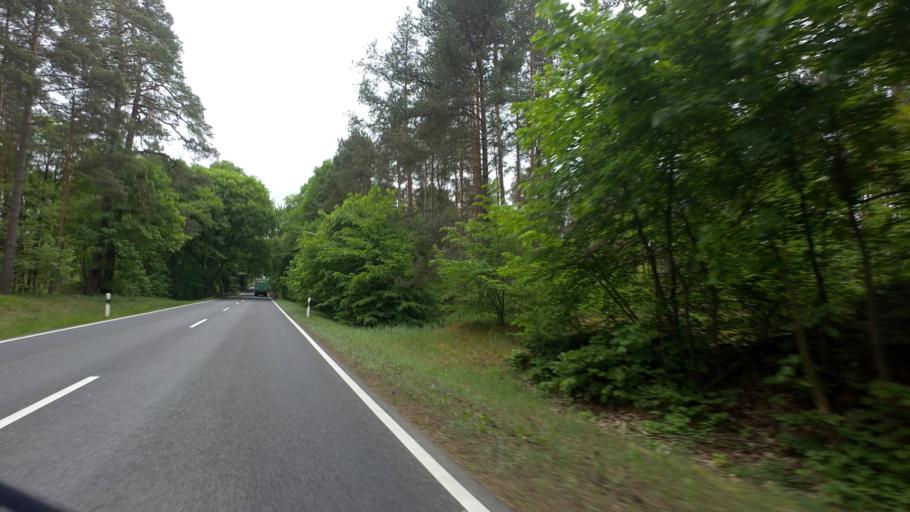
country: DE
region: Brandenburg
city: Furstenberg
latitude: 53.2223
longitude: 13.1223
